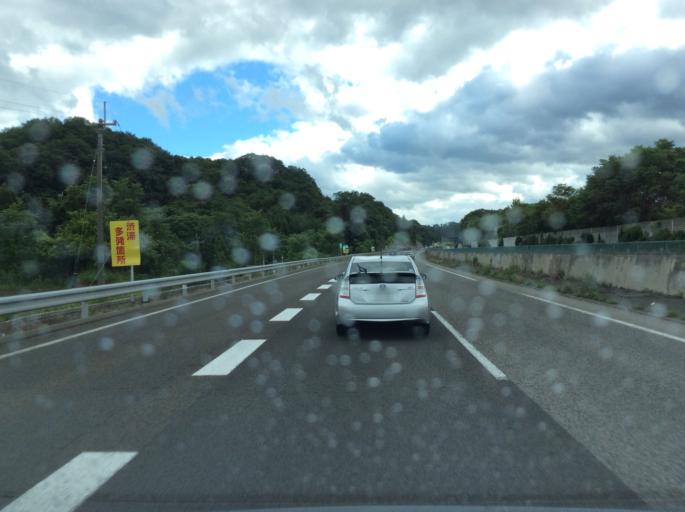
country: JP
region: Fukushima
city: Fukushima-shi
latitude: 37.7029
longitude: 140.4507
